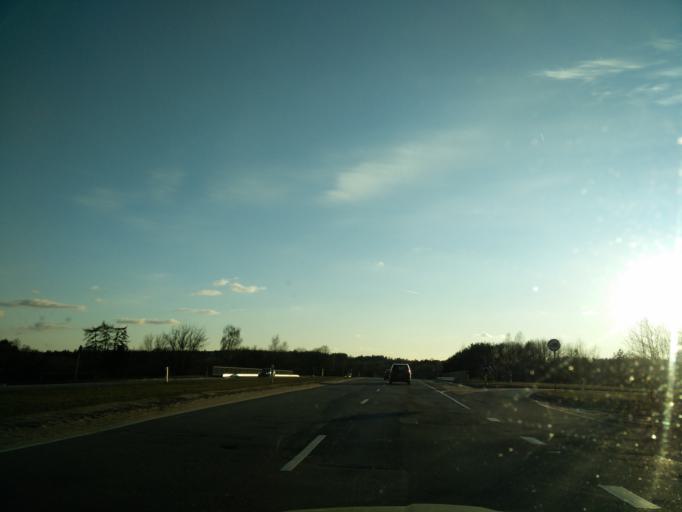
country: LT
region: Vilnius County
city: Rasos
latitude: 54.6927
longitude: 25.3457
